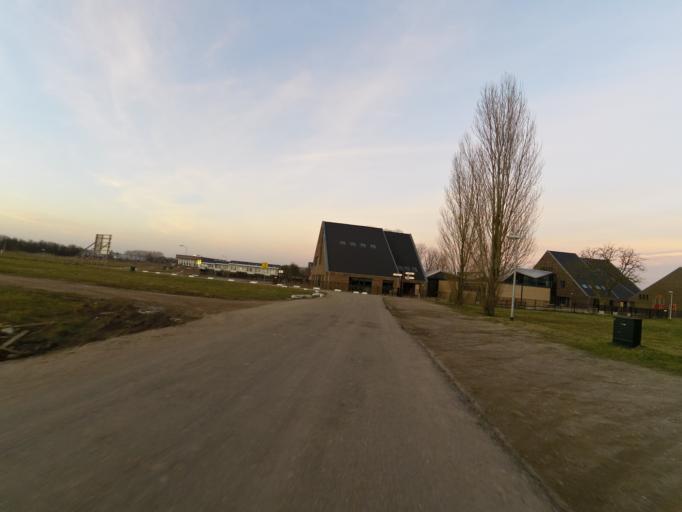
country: NL
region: Gelderland
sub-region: Gemeente Zevenaar
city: Zevenaar
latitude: 51.9187
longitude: 6.1006
